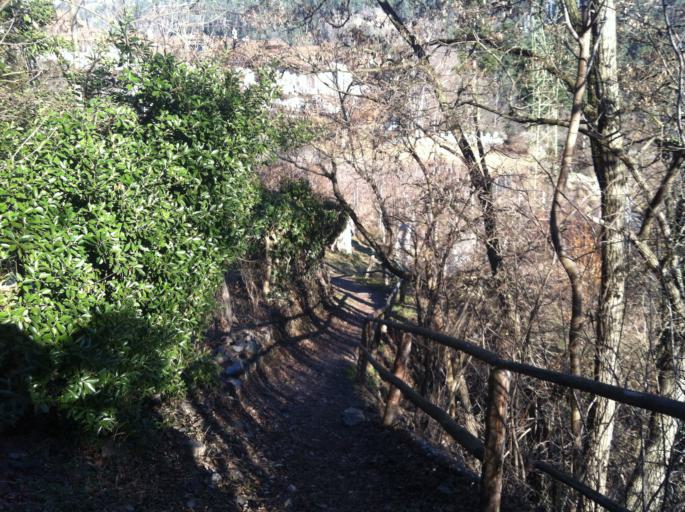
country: IT
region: Trentino-Alto Adige
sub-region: Bolzano
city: Bressanone
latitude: 46.7192
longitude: 11.6667
